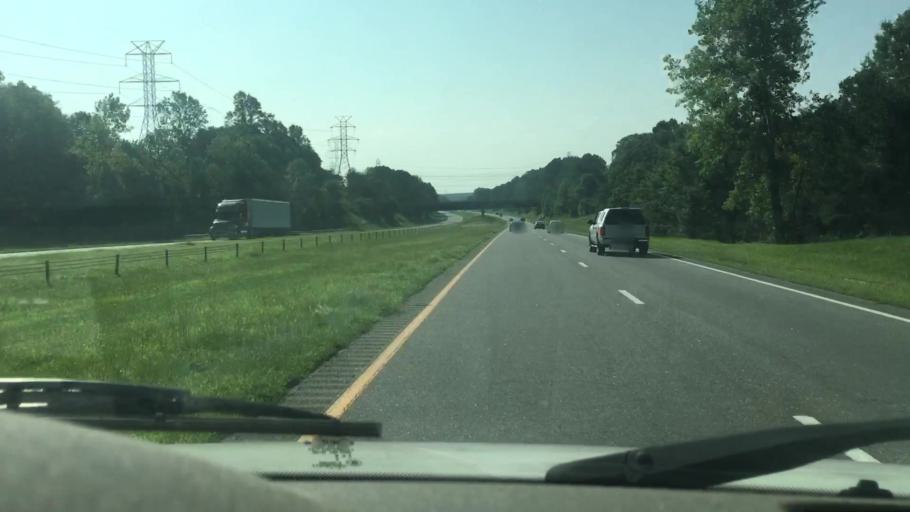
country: US
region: North Carolina
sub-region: Lincoln County
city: Lowesville
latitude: 35.3616
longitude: -80.9861
